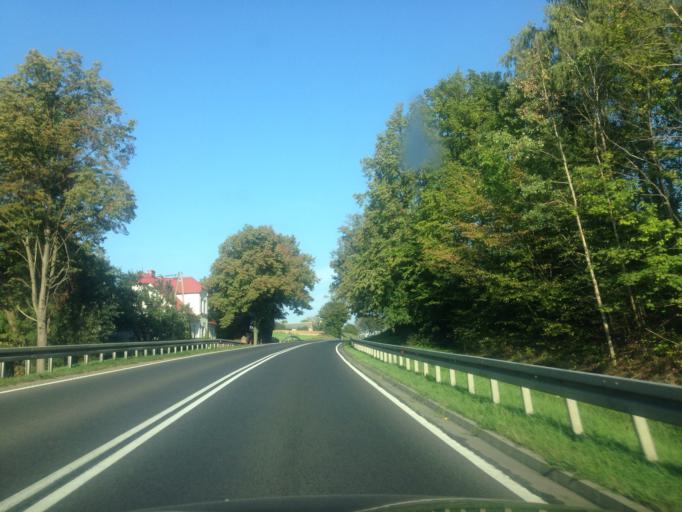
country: PL
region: Kujawsko-Pomorskie
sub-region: Powiat brodnicki
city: Brzozie
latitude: 53.3257
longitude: 19.5417
